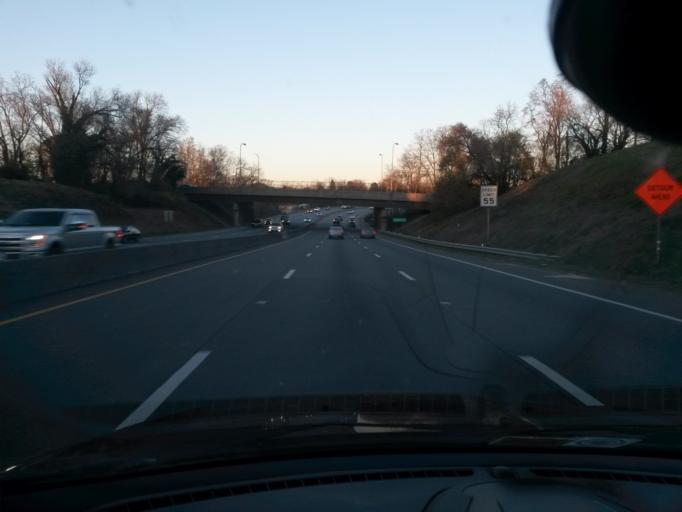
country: US
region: Virginia
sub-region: City of Roanoke
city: Roanoke
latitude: 37.2550
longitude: -79.9538
